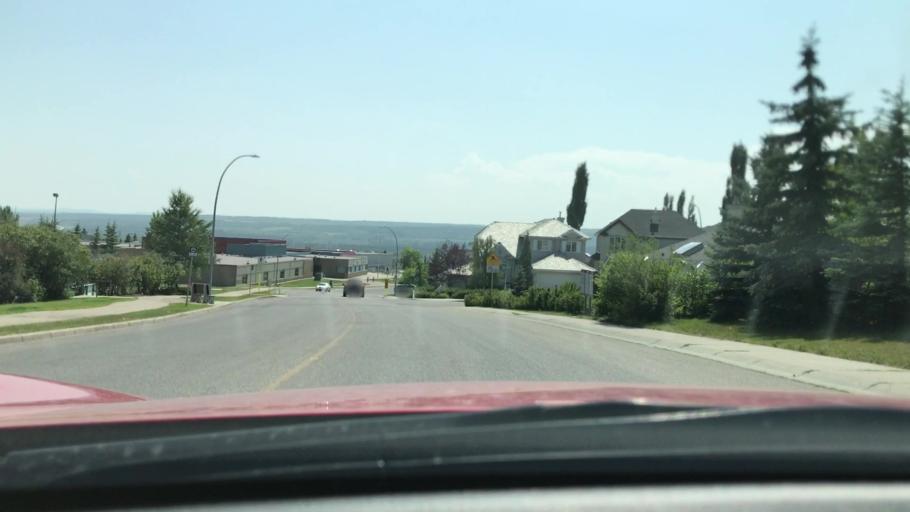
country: CA
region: Alberta
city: Calgary
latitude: 51.0259
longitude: -114.1804
